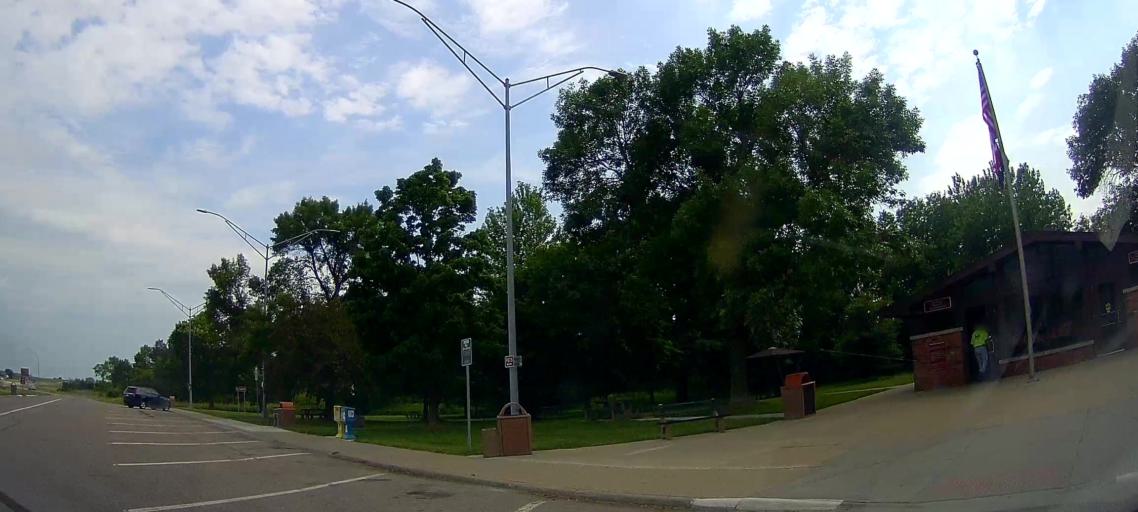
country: US
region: Iowa
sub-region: Monona County
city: Onawa
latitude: 41.9925
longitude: -96.1114
